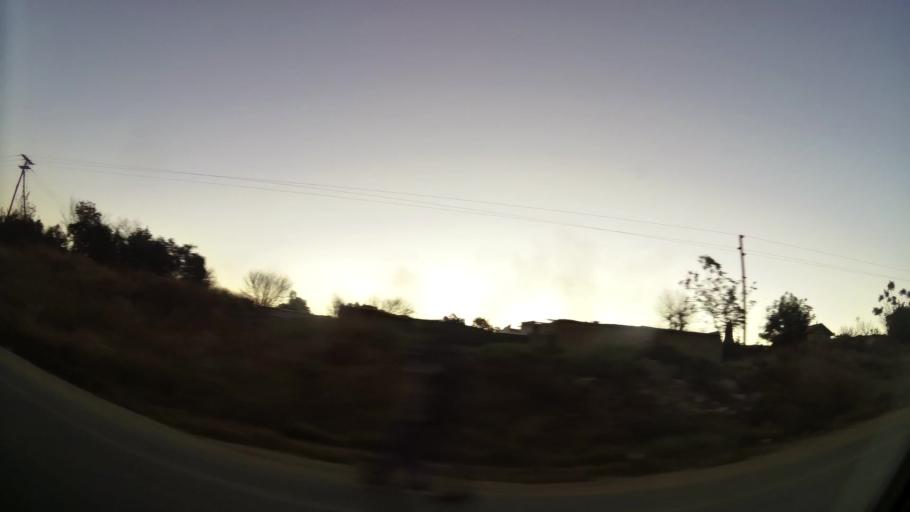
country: ZA
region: Gauteng
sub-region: City of Johannesburg Metropolitan Municipality
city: Diepsloot
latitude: -25.9200
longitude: 28.0233
